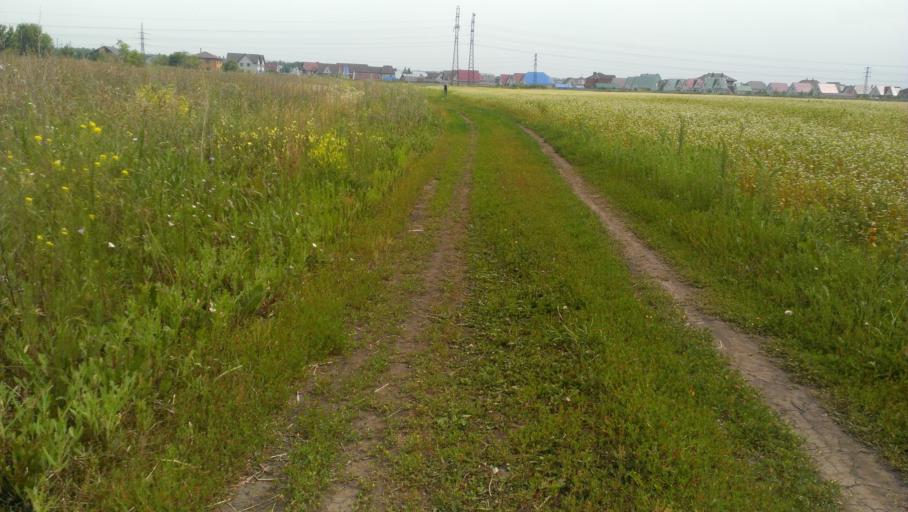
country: RU
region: Altai Krai
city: Novosilikatnyy
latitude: 53.3745
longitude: 83.6470
